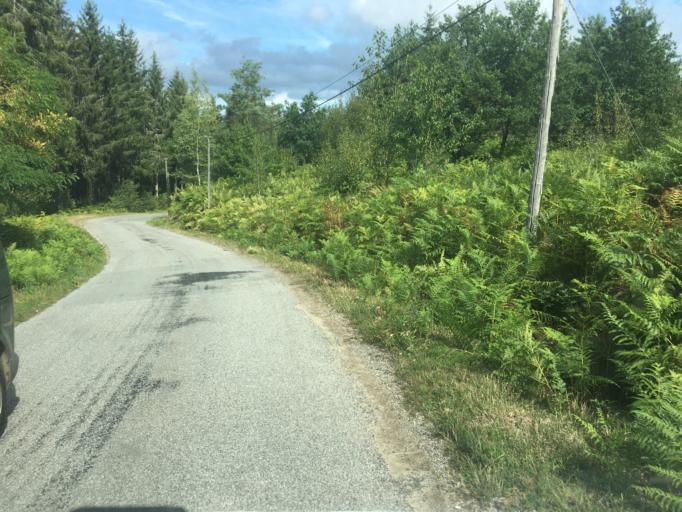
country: FR
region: Auvergne
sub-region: Departement du Cantal
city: Champagnac
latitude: 45.4213
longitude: 2.4065
